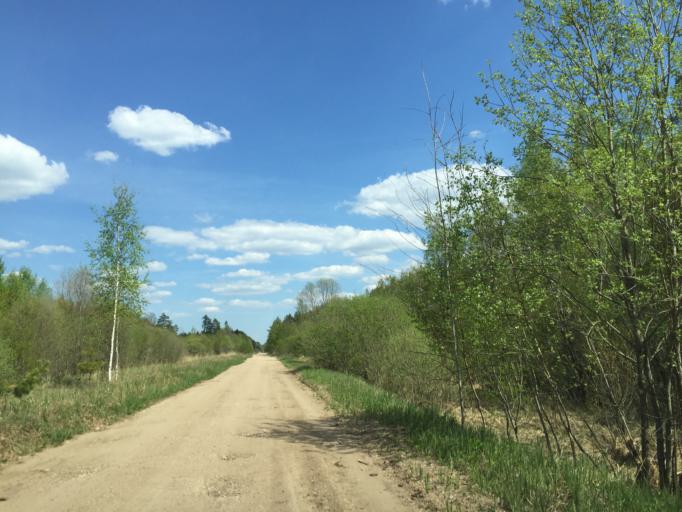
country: LV
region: Limbazu Rajons
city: Limbazi
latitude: 57.3963
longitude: 24.5815
